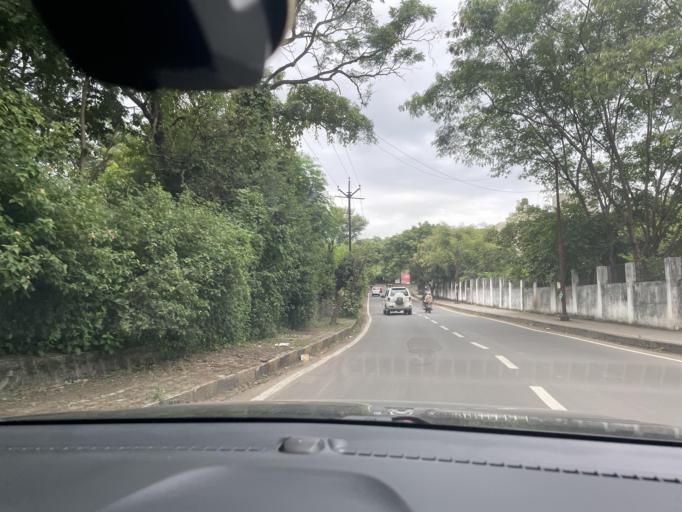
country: IN
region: Maharashtra
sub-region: Pune Division
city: Shivaji Nagar
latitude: 18.5371
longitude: 73.8099
